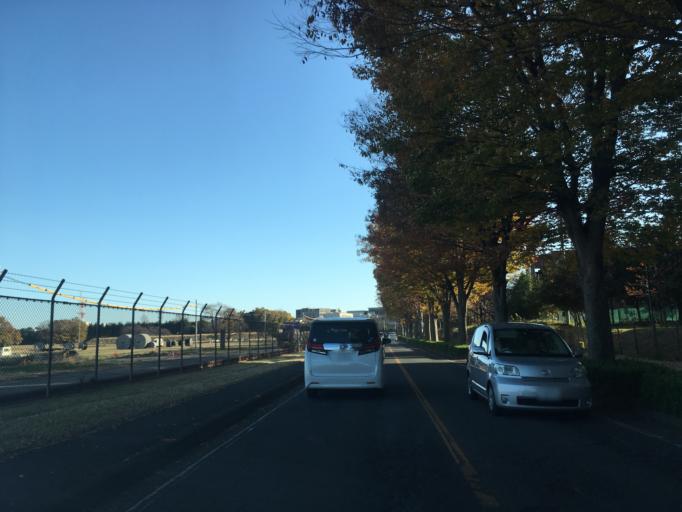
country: JP
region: Saitama
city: Tokorozawa
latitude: 35.8057
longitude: 139.4702
